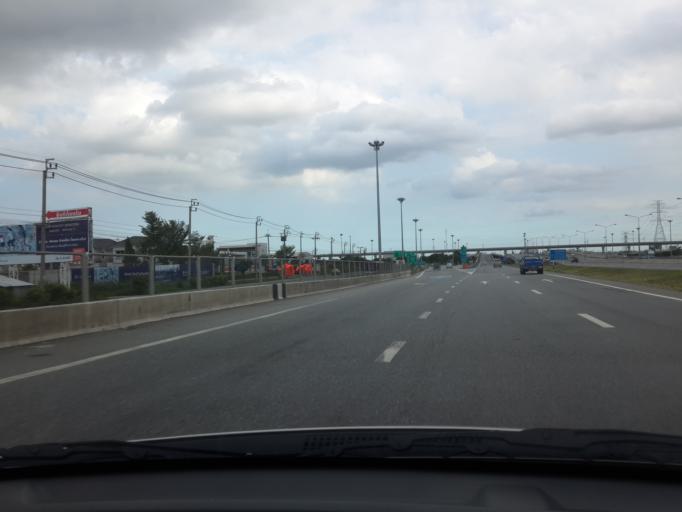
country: TH
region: Bangkok
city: Saphan Sung
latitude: 13.7394
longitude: 100.7031
